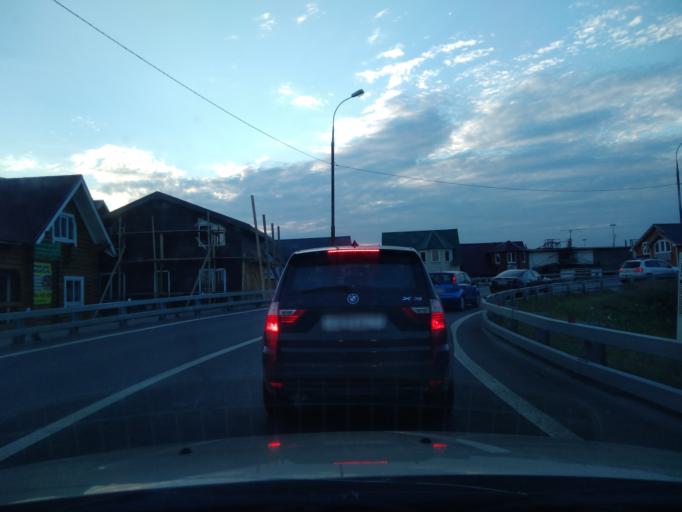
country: RU
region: Moscow
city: Strogino
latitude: 55.8072
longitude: 37.3866
